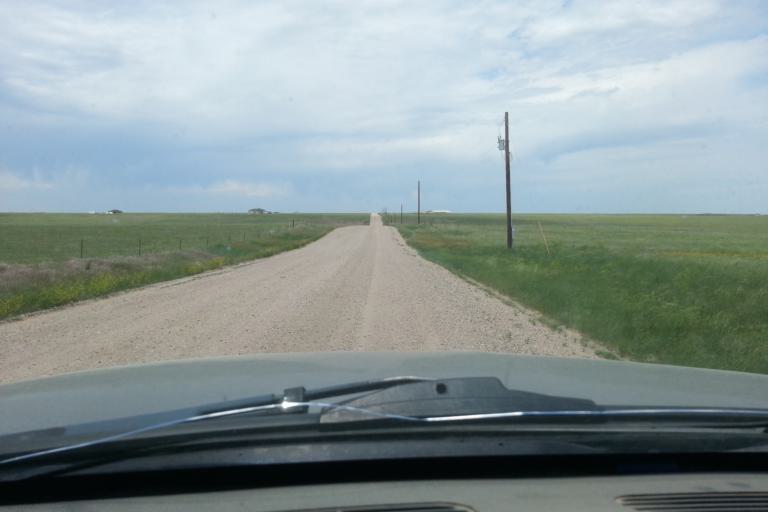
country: US
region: Wyoming
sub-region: Laramie County
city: Fox Farm-College
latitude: 41.0820
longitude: -104.5230
